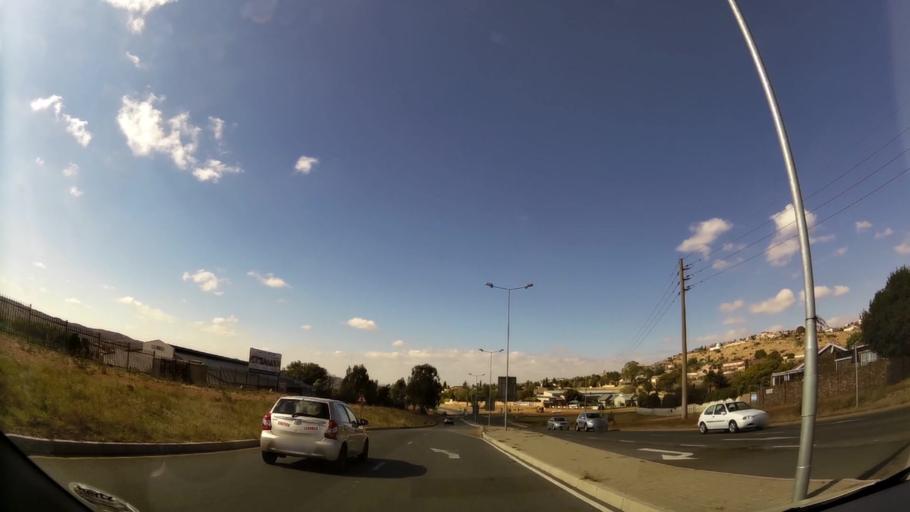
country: ZA
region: Gauteng
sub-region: West Rand District Municipality
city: Krugersdorp
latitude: -26.0849
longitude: 27.8074
